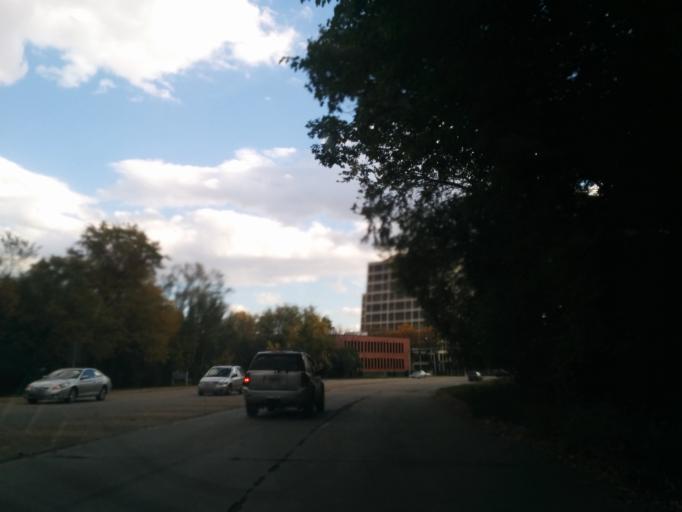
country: US
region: Illinois
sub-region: Cook County
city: Park Ridge
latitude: 41.9893
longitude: -87.8473
